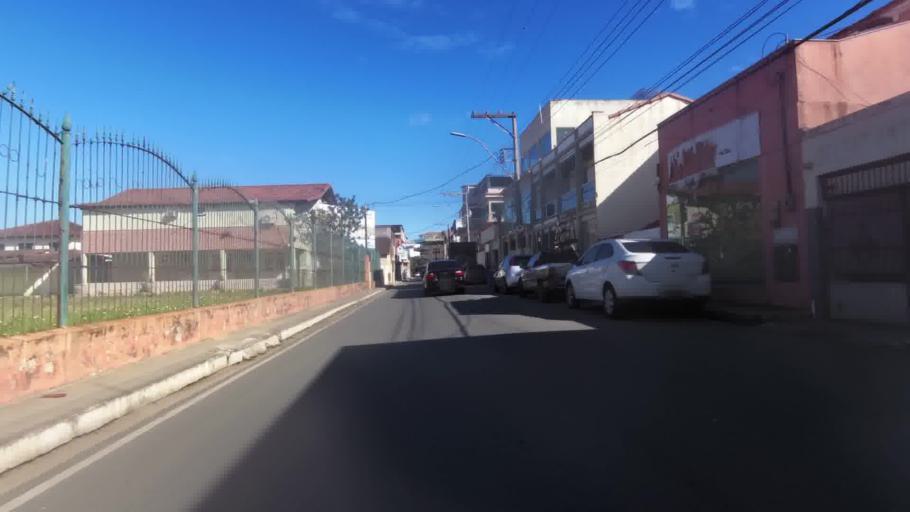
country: BR
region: Espirito Santo
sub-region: Piuma
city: Piuma
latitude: -20.8068
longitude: -40.6478
